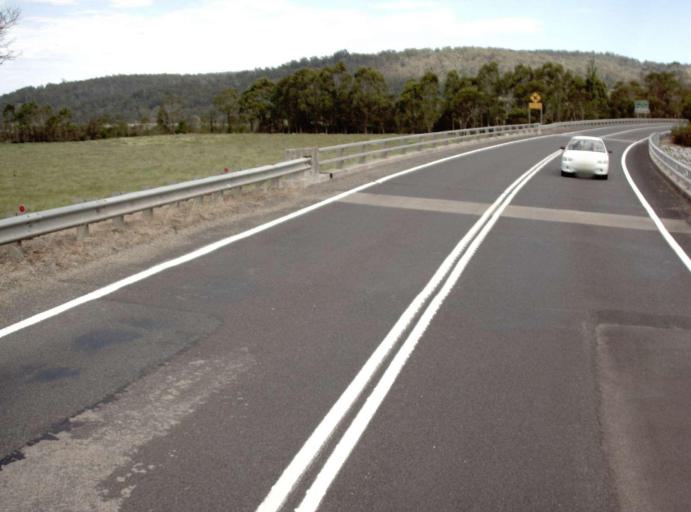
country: AU
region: New South Wales
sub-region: Bega Valley
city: Eden
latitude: -37.4719
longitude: 149.5931
